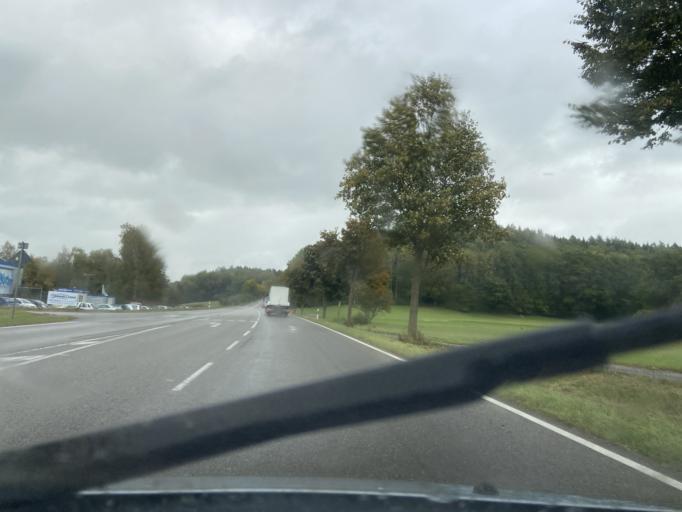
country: DE
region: Baden-Wuerttemberg
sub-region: Tuebingen Region
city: Messkirch
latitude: 47.9969
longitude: 9.1288
